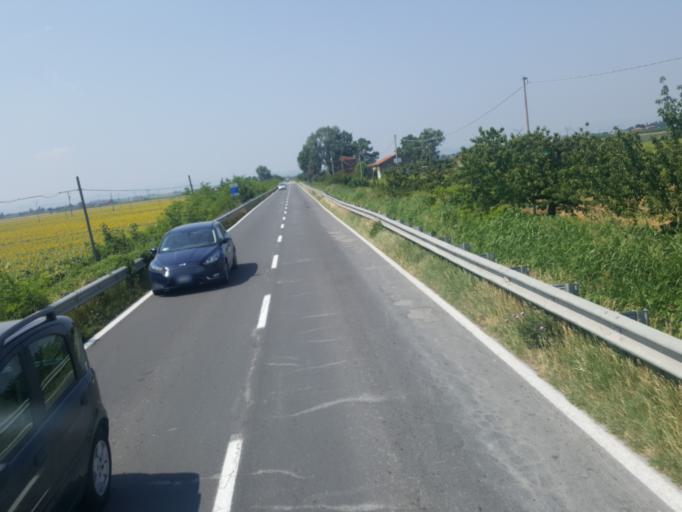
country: IT
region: Emilia-Romagna
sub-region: Provincia di Bologna
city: Sesto Imolese
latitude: 44.4658
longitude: 11.7649
